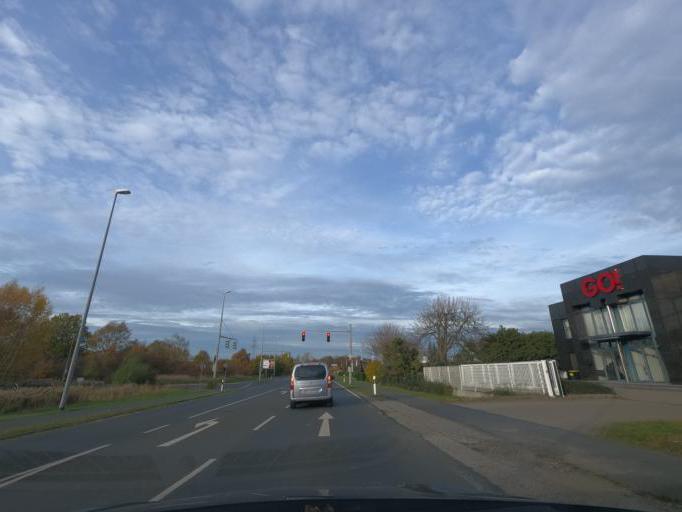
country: DE
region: Lower Saxony
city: Cremlingen
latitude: 52.2930
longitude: 10.5977
